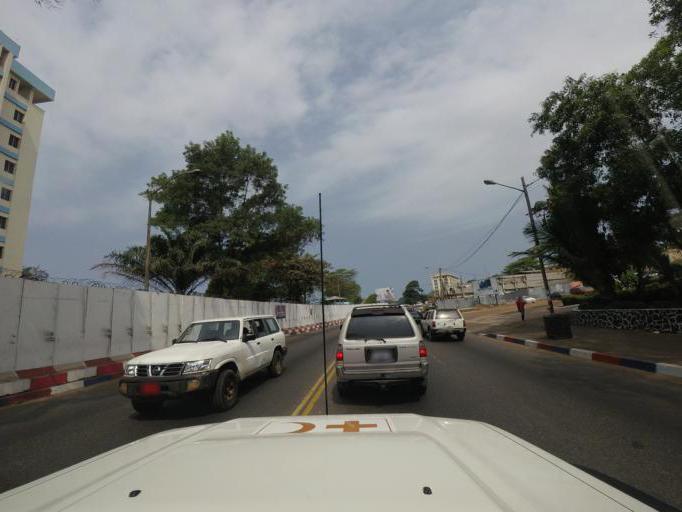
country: LR
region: Montserrado
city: Monrovia
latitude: 6.2951
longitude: -10.7939
